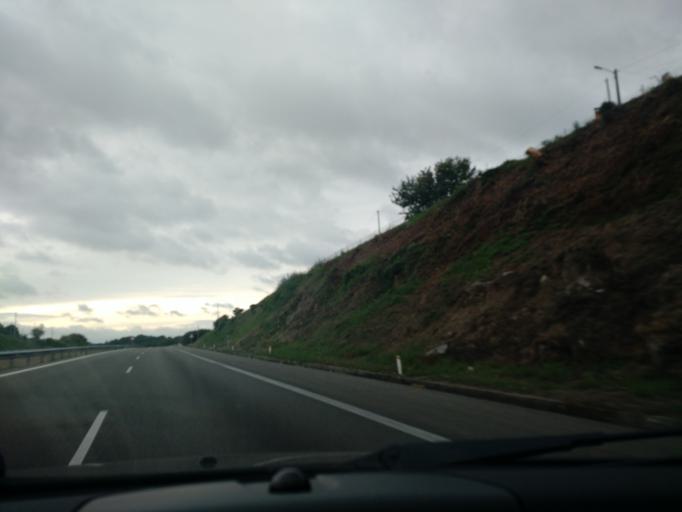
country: ES
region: Galicia
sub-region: Provincia da Coruna
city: Cambre
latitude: 43.2992
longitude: -8.3162
